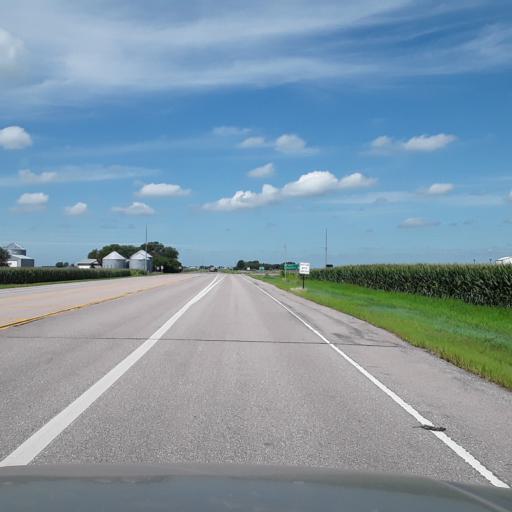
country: US
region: Nebraska
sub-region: York County
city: York
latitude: 40.9017
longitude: -97.4031
